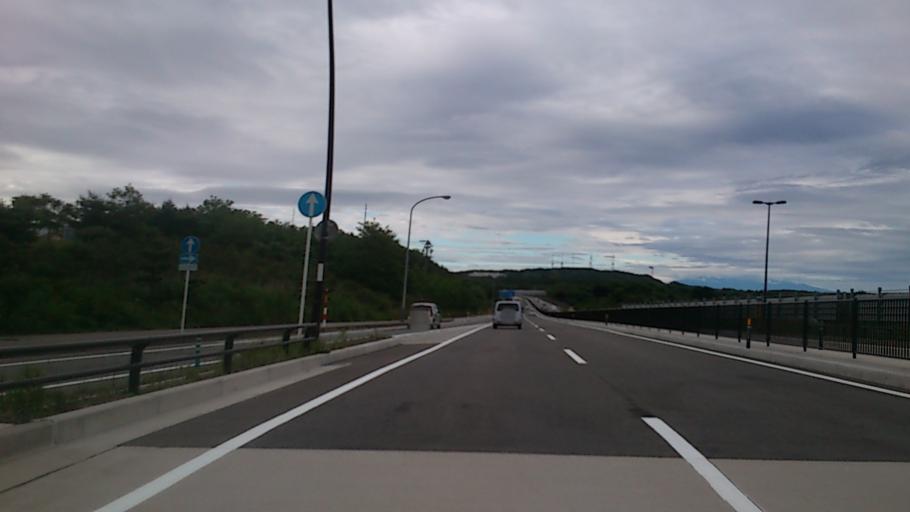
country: JP
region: Akita
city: Akita Shi
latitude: 39.6973
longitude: 140.0688
